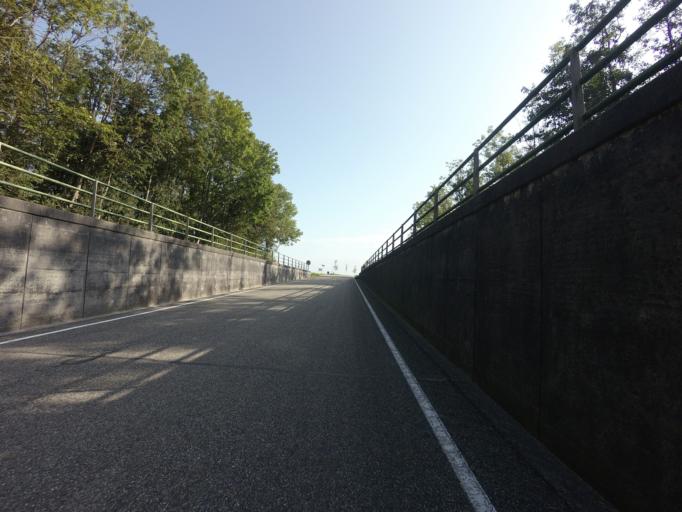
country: NL
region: Friesland
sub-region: Gemeente Franekeradeel
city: Franeker
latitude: 53.2010
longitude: 5.5786
